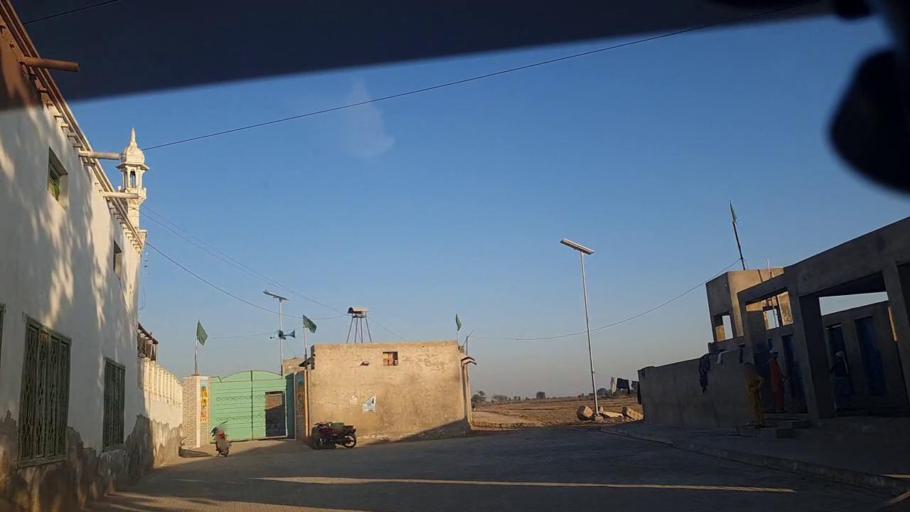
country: PK
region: Sindh
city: Khanpur
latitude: 27.8650
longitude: 69.4261
